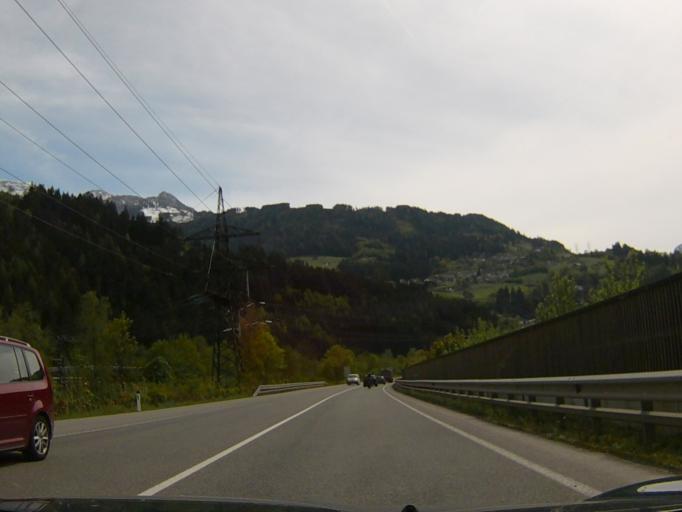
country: AT
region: Tyrol
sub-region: Politischer Bezirk Schwaz
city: Zell am Ziller
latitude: 47.2347
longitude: 11.8962
